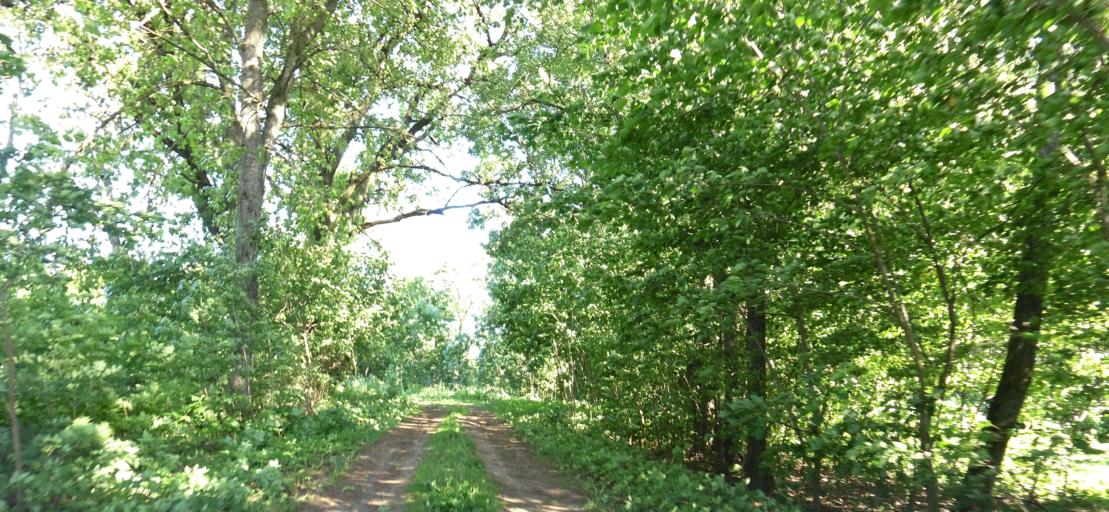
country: LT
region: Panevezys
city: Pasvalys
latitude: 56.1479
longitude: 24.4573
